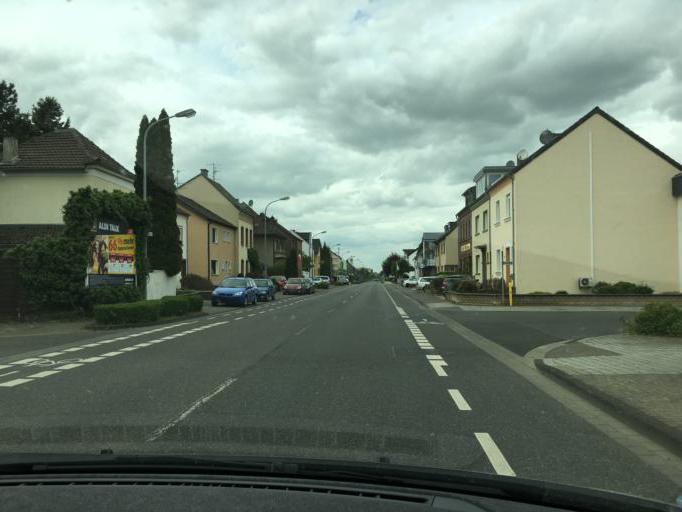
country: DE
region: North Rhine-Westphalia
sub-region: Regierungsbezirk Koln
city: Euskirchen
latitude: 50.6515
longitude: 6.8242
